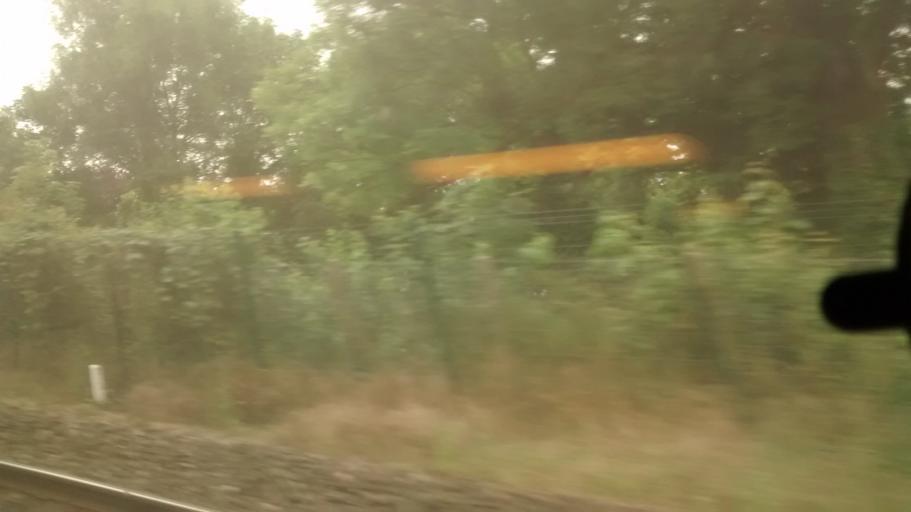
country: FR
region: Ile-de-France
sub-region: Departement de l'Essonne
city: Wissous
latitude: 48.7397
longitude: 2.3358
